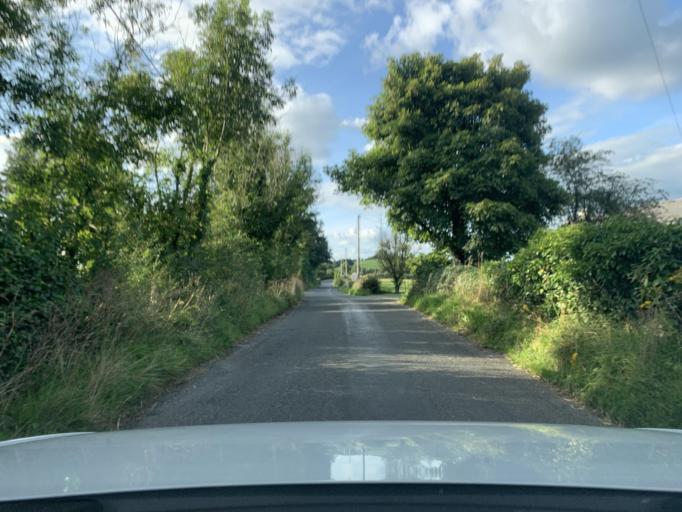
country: IE
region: Connaught
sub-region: Roscommon
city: Boyle
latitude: 54.0843
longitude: -8.3722
